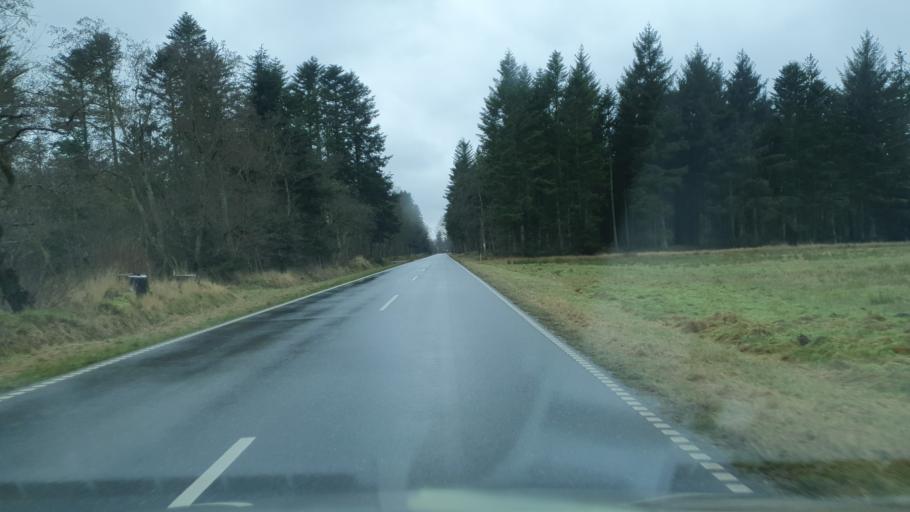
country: DK
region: North Denmark
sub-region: Jammerbugt Kommune
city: Fjerritslev
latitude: 57.1241
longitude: 9.1291
